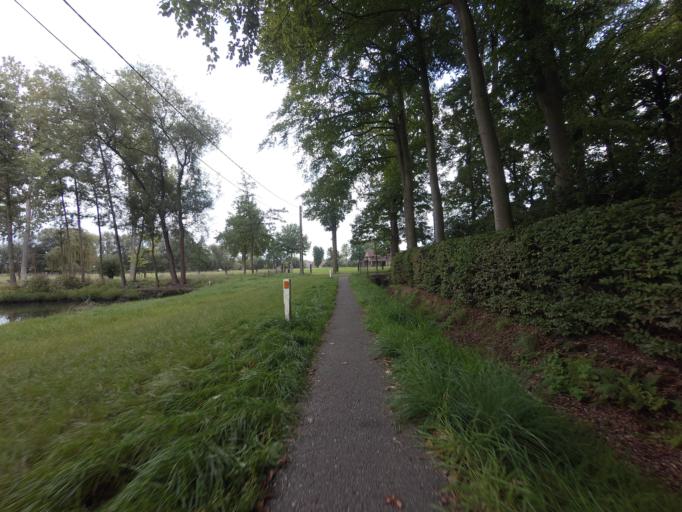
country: BE
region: Flanders
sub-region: Provincie Vlaams-Brabant
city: Londerzeel
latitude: 51.0184
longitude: 4.3314
